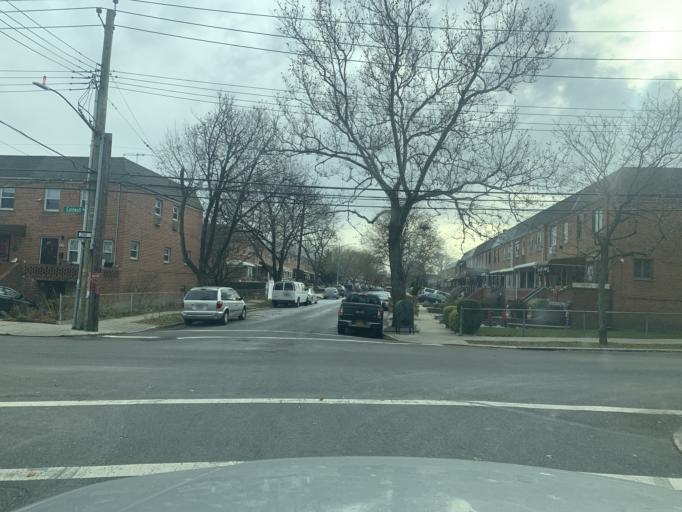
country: US
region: New York
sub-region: Kings County
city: East New York
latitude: 40.7250
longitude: -73.8842
